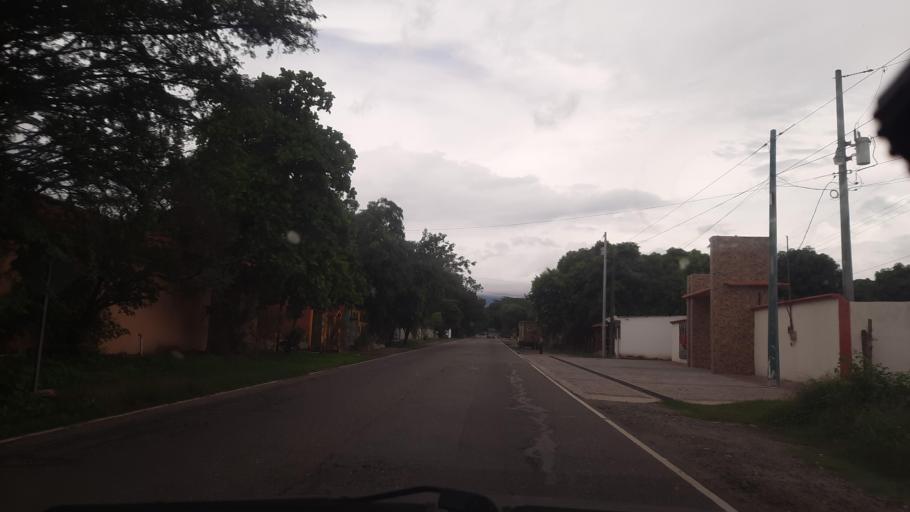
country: GT
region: Zacapa
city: San Jorge
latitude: 14.9079
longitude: -89.5279
